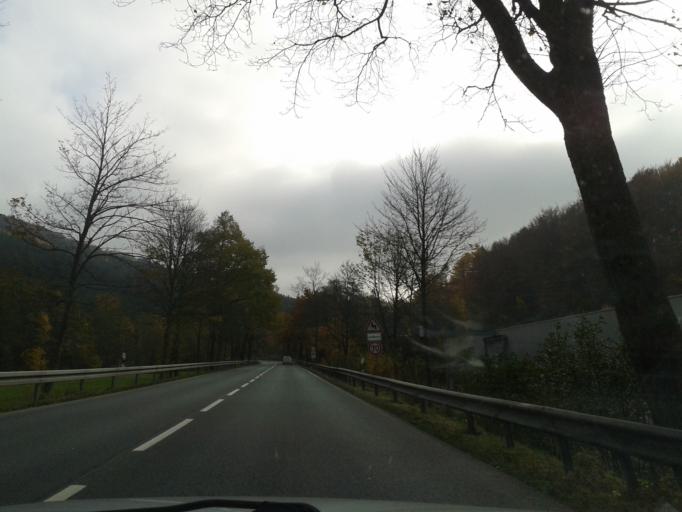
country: DE
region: North Rhine-Westphalia
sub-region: Regierungsbezirk Arnsberg
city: Olsberg
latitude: 51.2804
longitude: 8.5139
